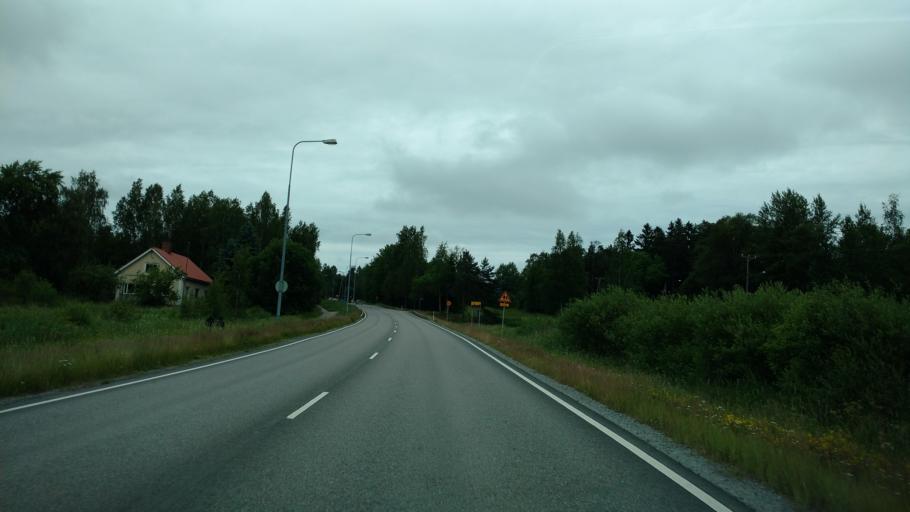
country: FI
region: Varsinais-Suomi
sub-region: Salo
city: Halikko
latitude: 60.4333
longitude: 23.0477
